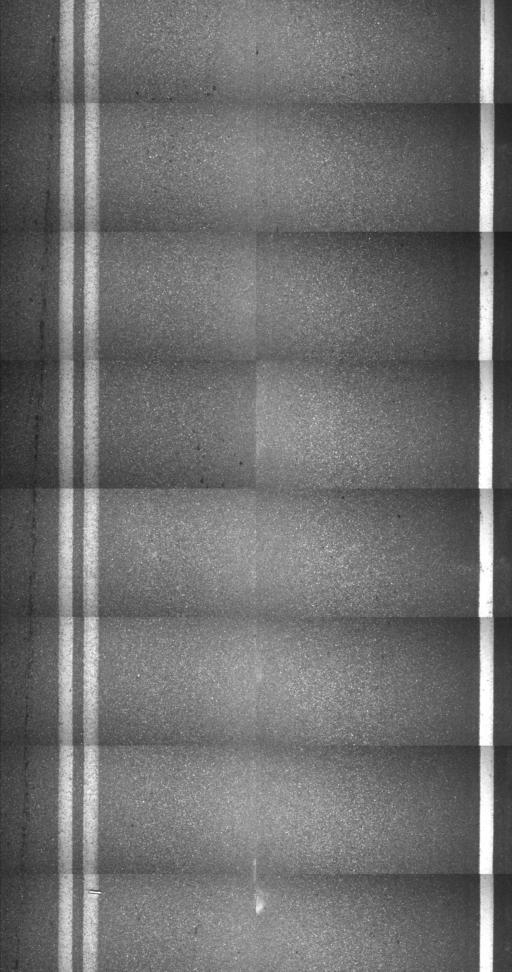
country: US
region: New York
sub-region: Clinton County
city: Cumberland Head
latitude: 44.6796
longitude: -73.3473
